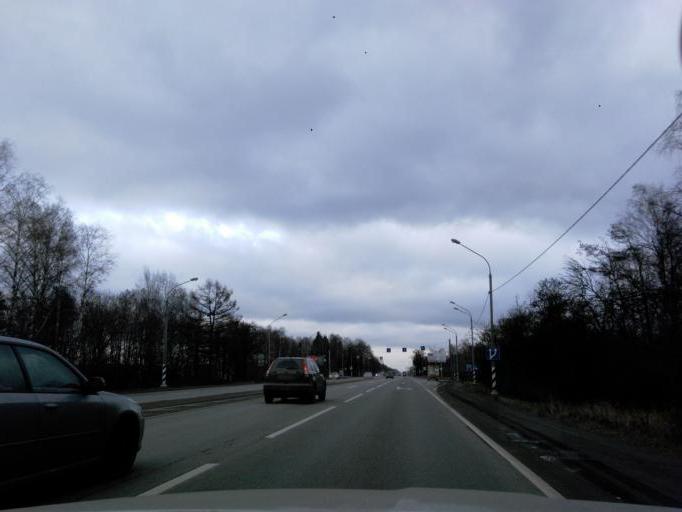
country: RU
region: Moskovskaya
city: Chashnikovo
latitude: 56.0245
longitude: 37.1814
